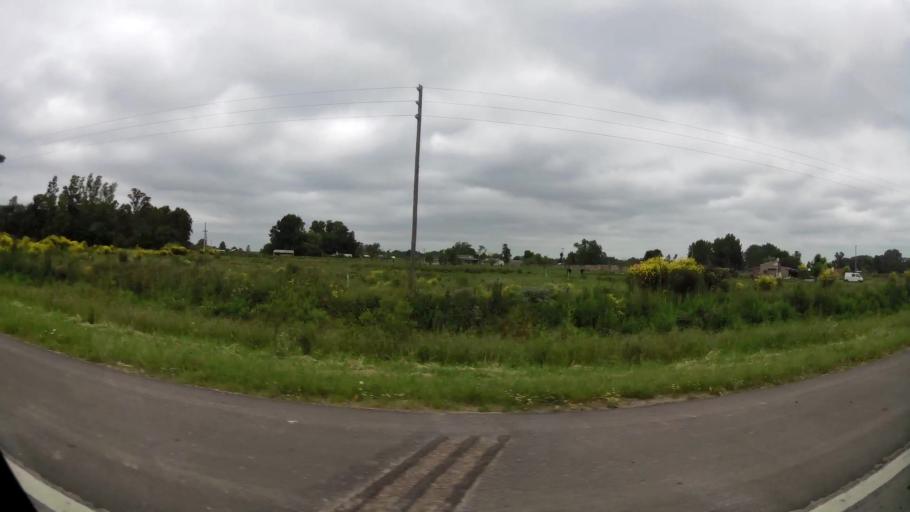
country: AR
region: Buenos Aires
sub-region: Partido de San Vicente
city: San Vicente
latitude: -35.0461
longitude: -58.4177
